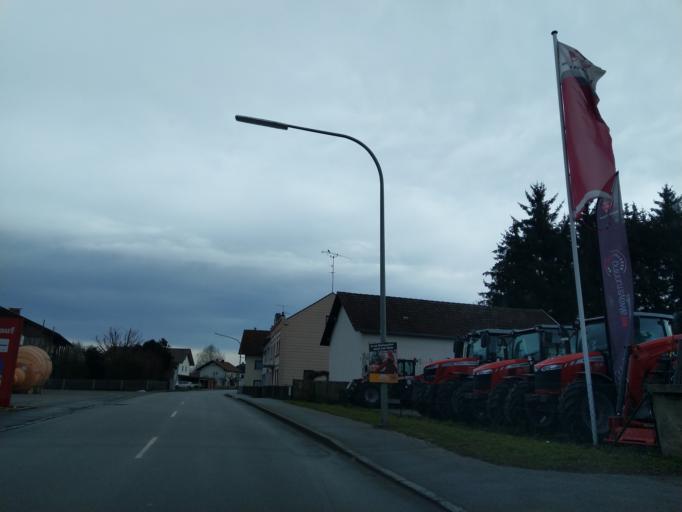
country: DE
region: Bavaria
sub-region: Lower Bavaria
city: Osterhofen
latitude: 48.6936
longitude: 13.0196
